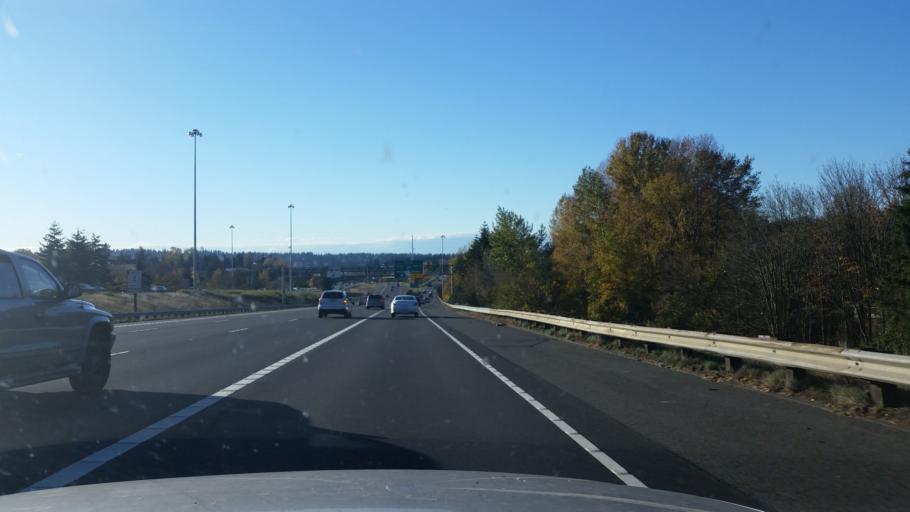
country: US
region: Washington
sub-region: King County
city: Eastgate
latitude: 47.5803
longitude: -122.1634
